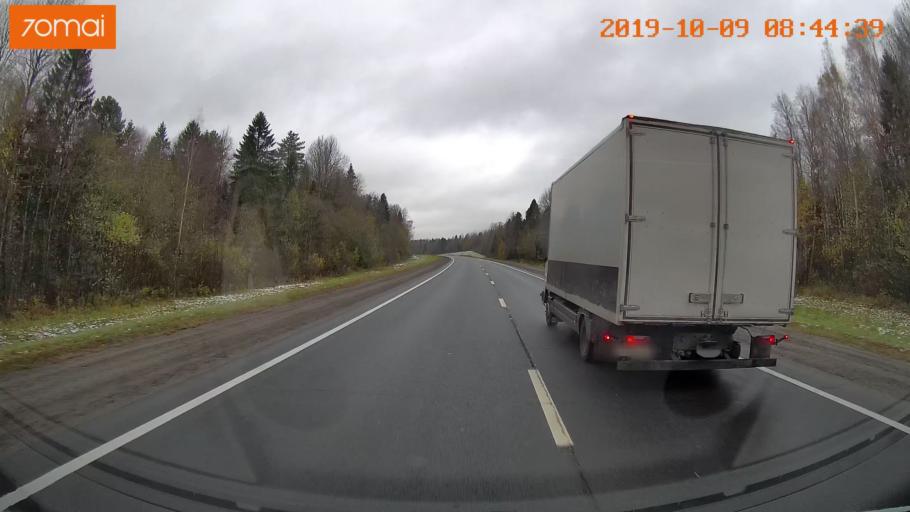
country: RU
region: Vologda
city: Gryazovets
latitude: 59.0392
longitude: 40.1057
